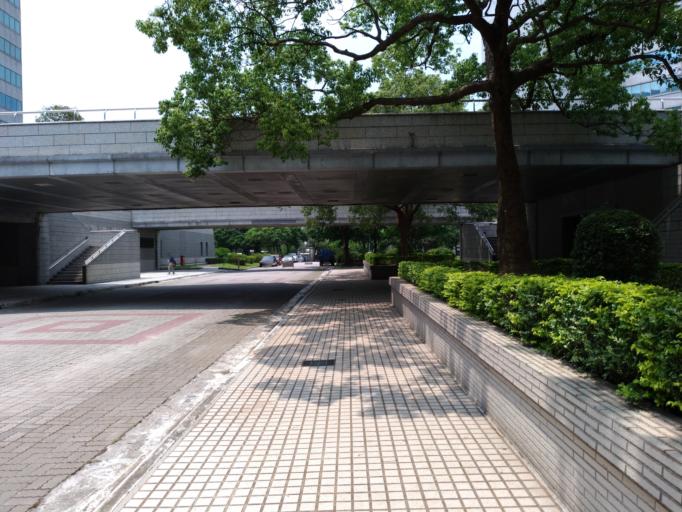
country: TW
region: Taiwan
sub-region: Hsinchu
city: Zhubei
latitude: 24.7739
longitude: 121.0446
